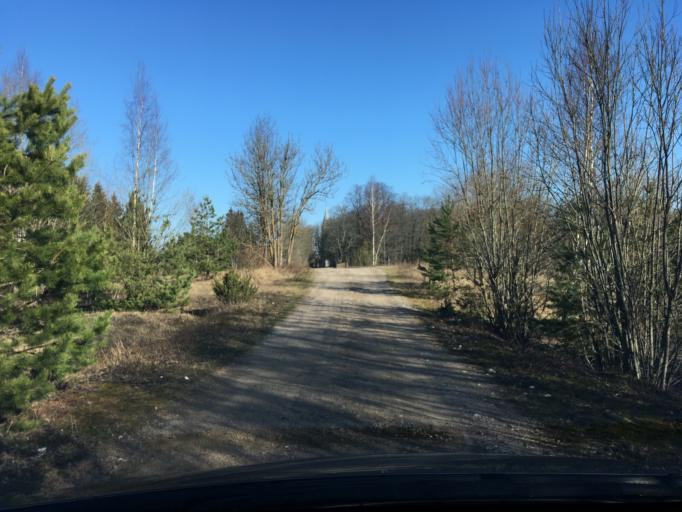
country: EE
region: Laeaene
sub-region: Lihula vald
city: Lihula
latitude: 58.6343
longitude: 23.6894
